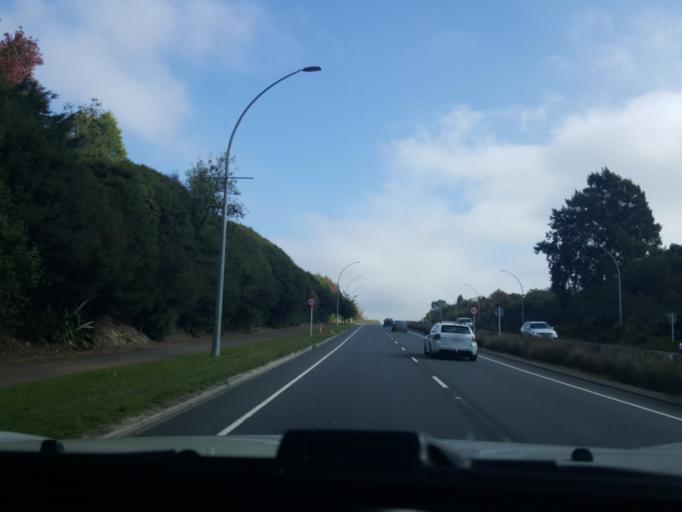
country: NZ
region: Waikato
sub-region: Hamilton City
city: Hamilton
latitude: -37.7456
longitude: 175.2481
